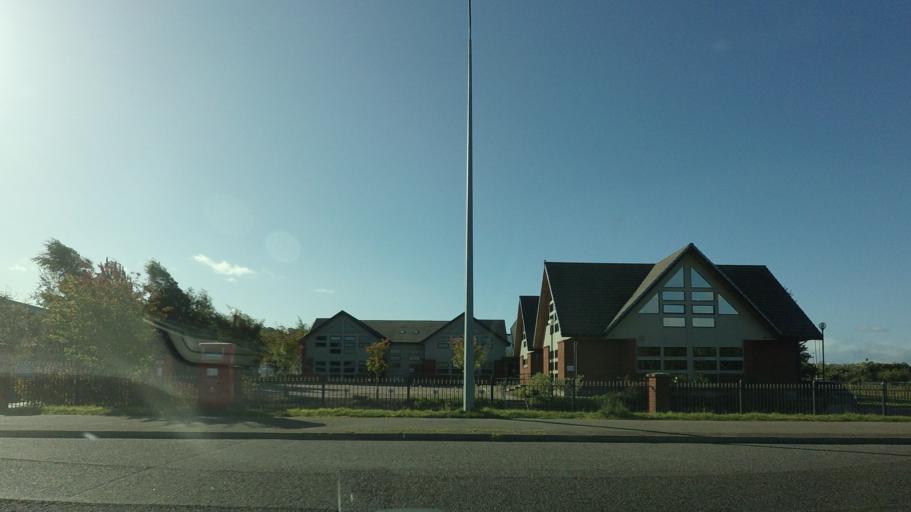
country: GB
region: Scotland
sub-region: Highland
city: Inverness
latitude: 57.4528
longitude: -4.2145
